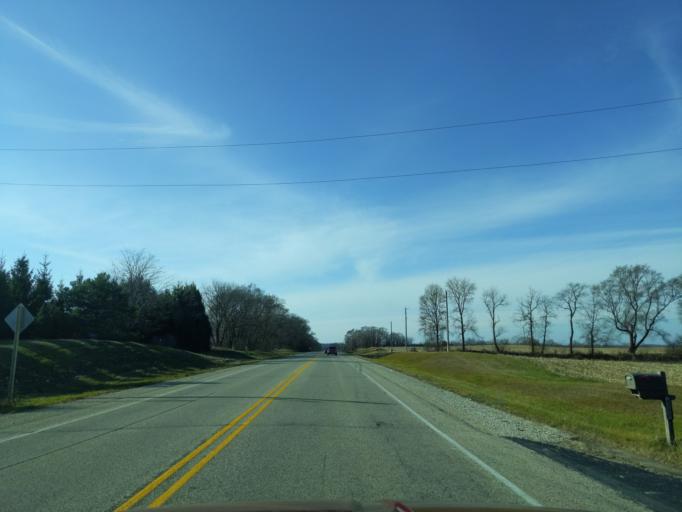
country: US
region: Wisconsin
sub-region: Rock County
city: Milton
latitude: 42.8246
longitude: -88.9640
